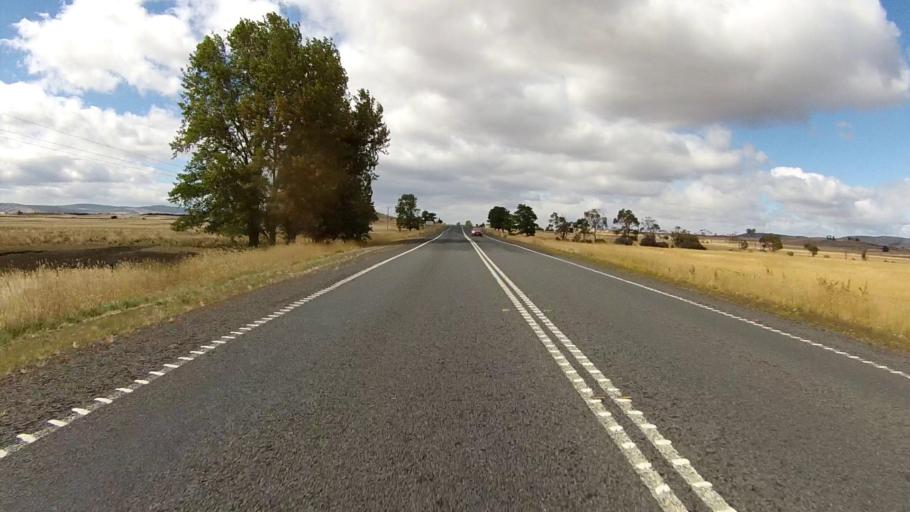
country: AU
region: Tasmania
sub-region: Northern Midlands
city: Evandale
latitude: -41.8658
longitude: 147.4580
